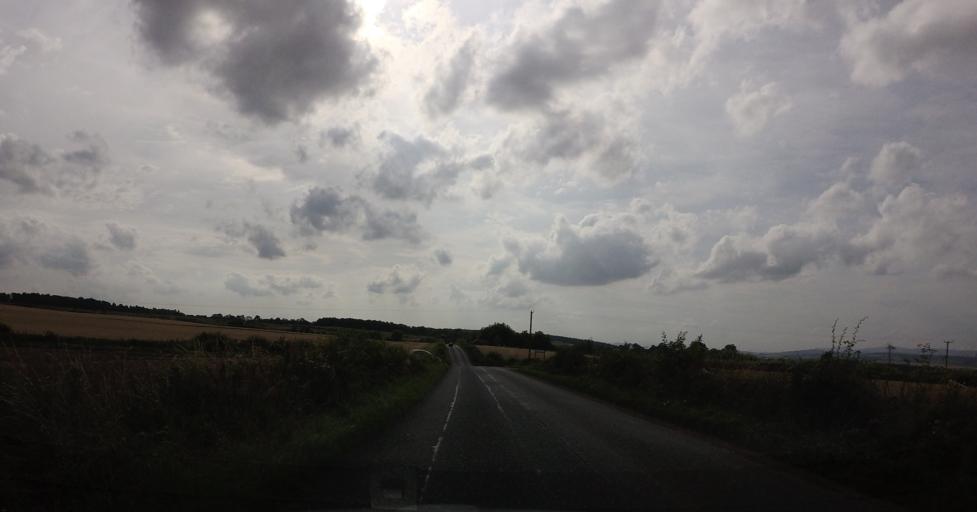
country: GB
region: Scotland
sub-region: Perth and Kinross
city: Methven
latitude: 56.3897
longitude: -3.5870
